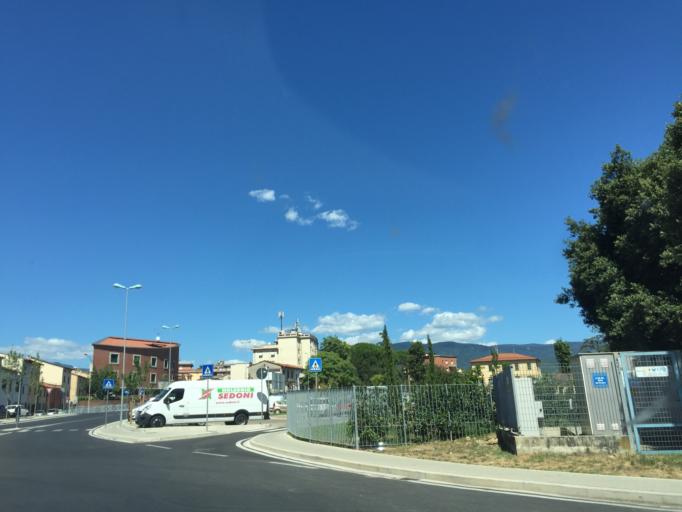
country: IT
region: Tuscany
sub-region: Provincia di Pistoia
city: Pistoia
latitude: 43.9242
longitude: 10.9185
